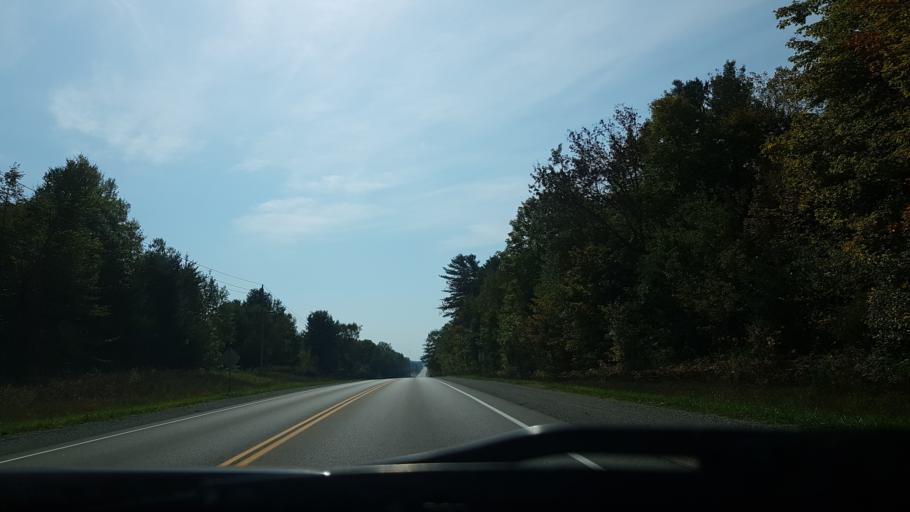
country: CA
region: Ontario
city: Orillia
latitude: 44.7250
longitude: -79.2864
